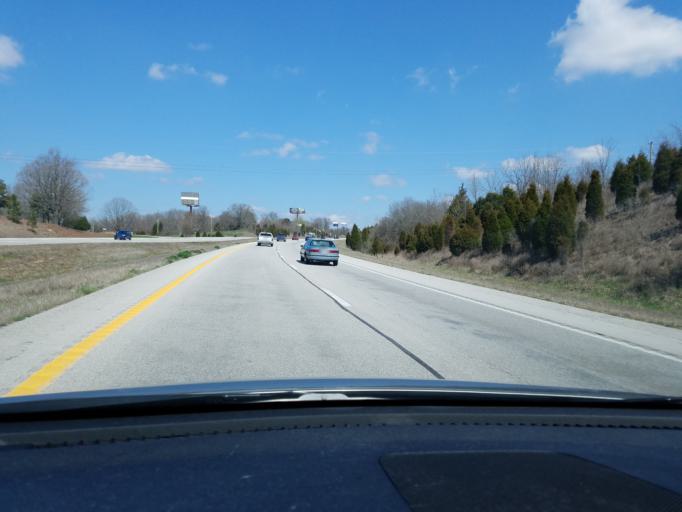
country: US
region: Missouri
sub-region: Taney County
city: Merriam Woods
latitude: 36.7966
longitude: -93.2264
